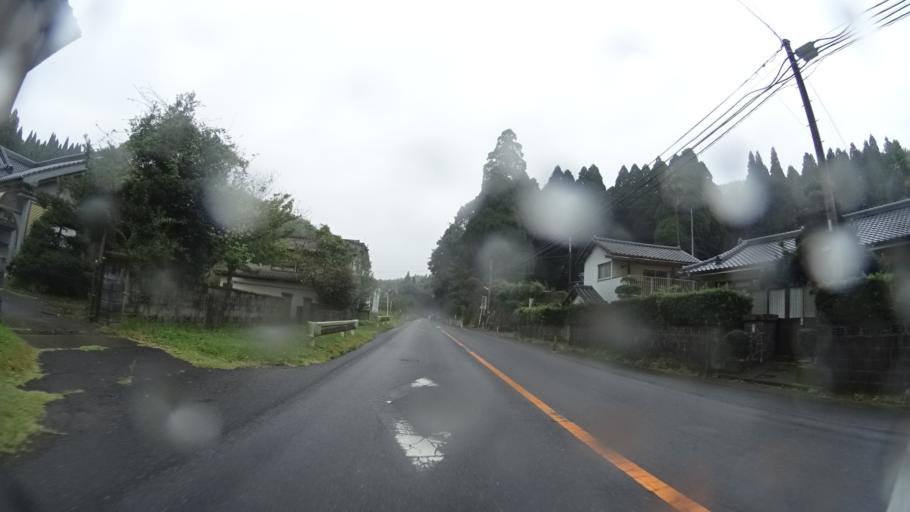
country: JP
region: Kagoshima
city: Kajiki
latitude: 31.8246
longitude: 130.6799
